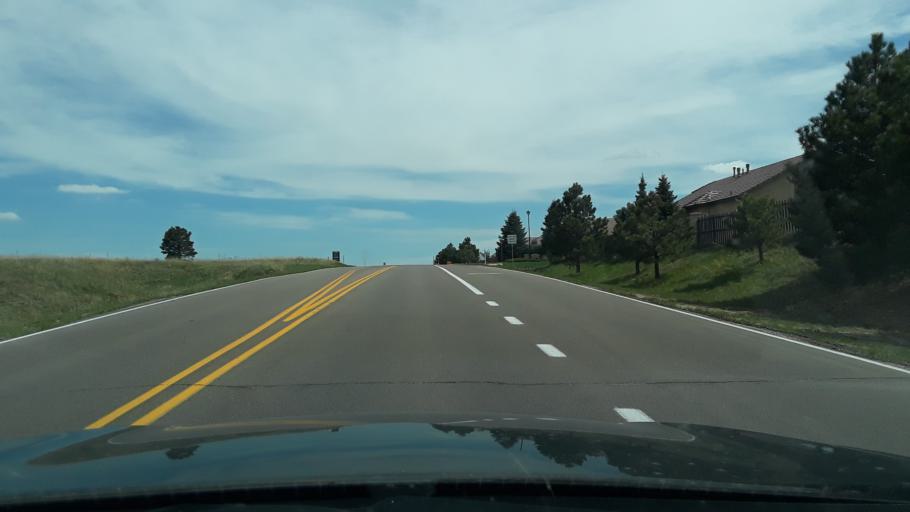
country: US
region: Colorado
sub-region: El Paso County
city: Monument
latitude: 39.0843
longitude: -104.8672
